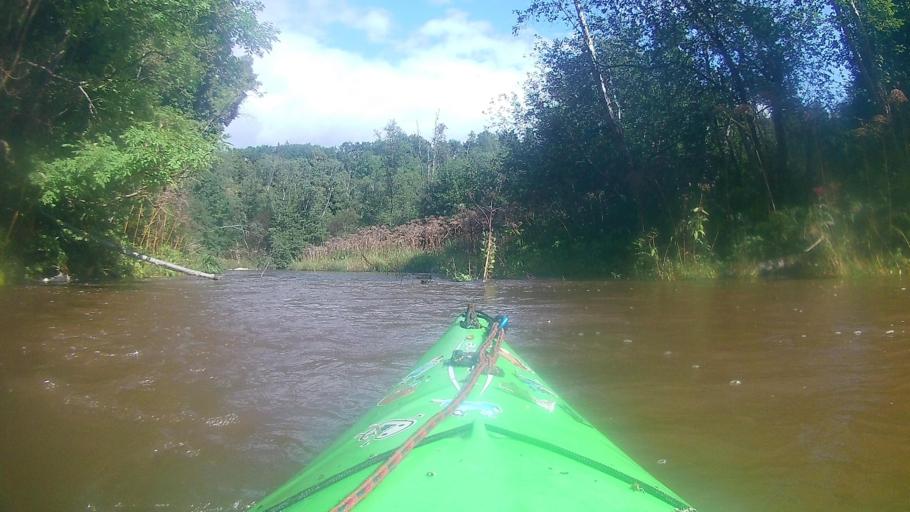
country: LV
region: Talsu Rajons
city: Sabile
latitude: 57.0067
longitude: 22.6177
